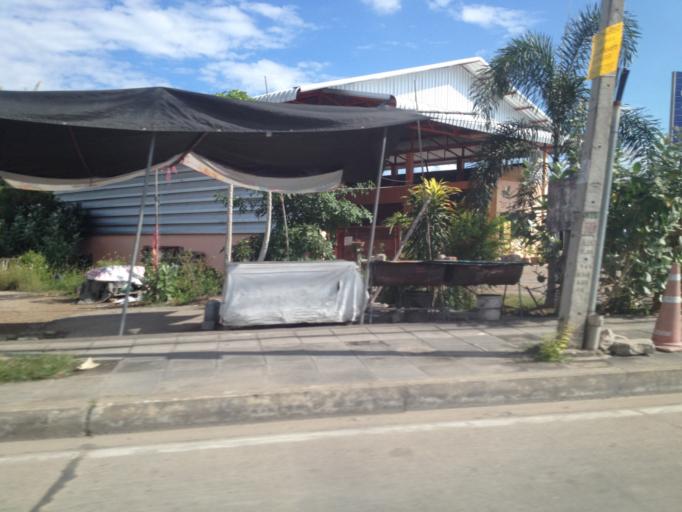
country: TH
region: Chiang Mai
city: Chiang Mai
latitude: 18.7515
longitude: 98.9653
